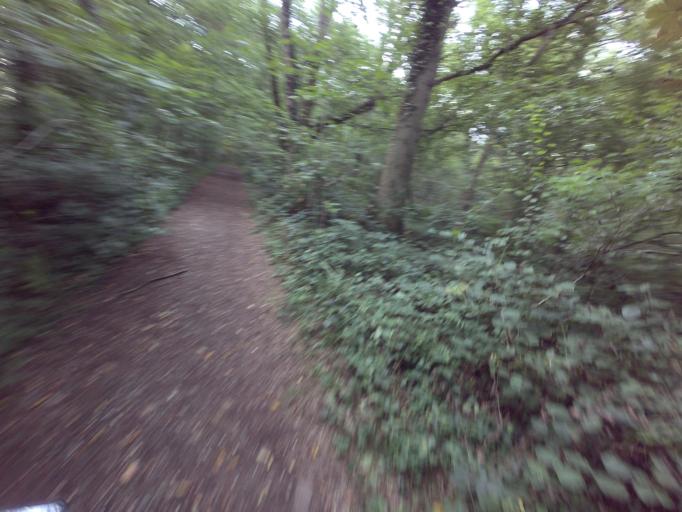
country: NL
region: Limburg
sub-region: Valkenburg aan de Geul
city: Valkenburg
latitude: 50.8527
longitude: 5.8381
